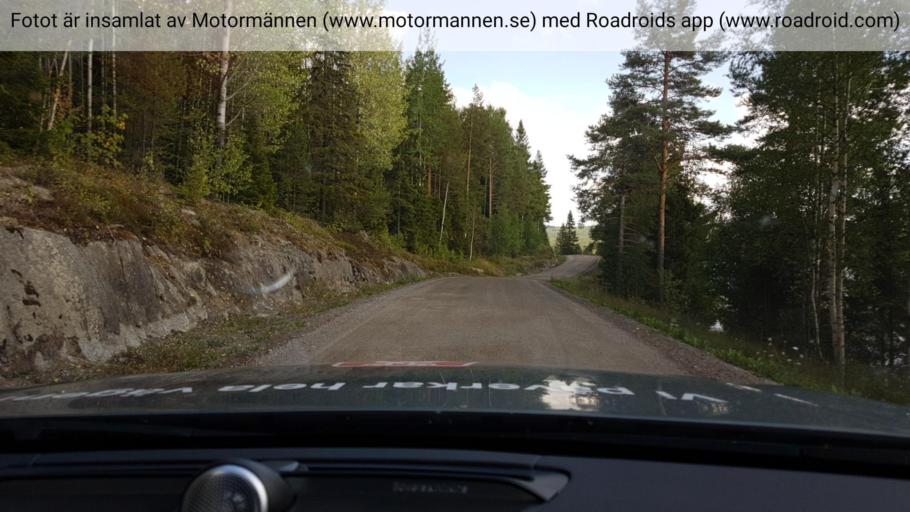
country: SE
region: Jaemtland
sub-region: Stroemsunds Kommun
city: Stroemsund
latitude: 63.9972
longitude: 15.9733
